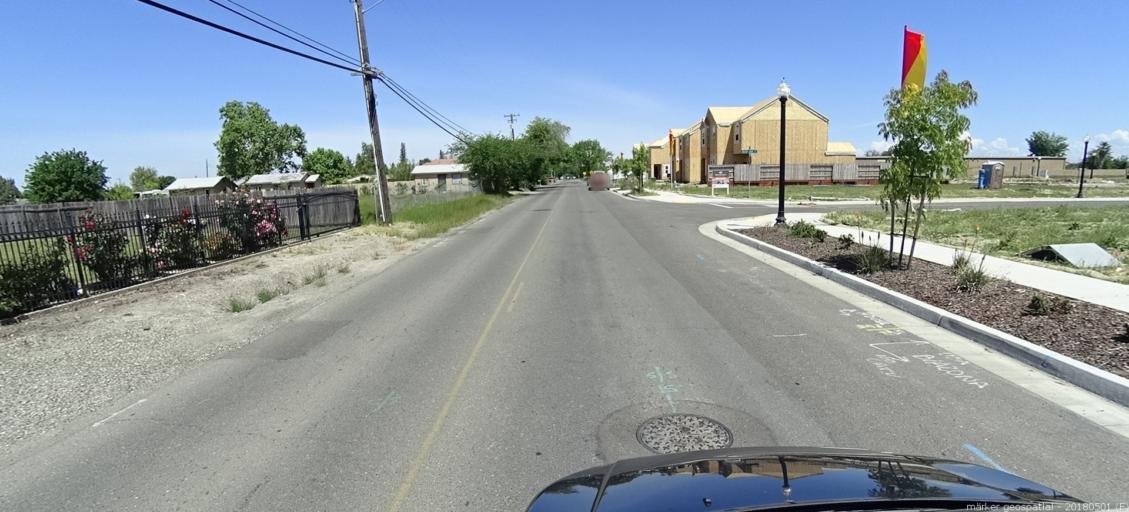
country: US
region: California
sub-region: Sacramento County
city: Rio Linda
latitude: 38.6482
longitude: -121.4384
